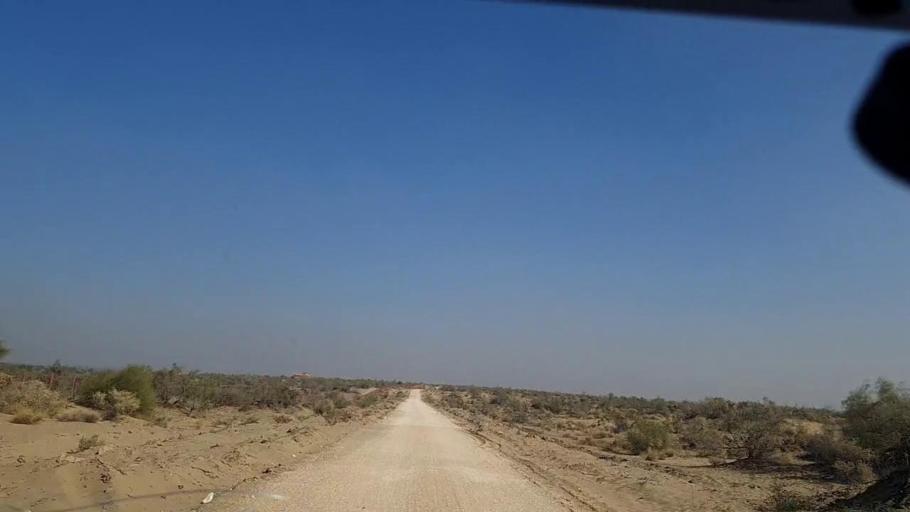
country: PK
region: Sindh
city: Khanpur
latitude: 27.5574
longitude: 69.3916
